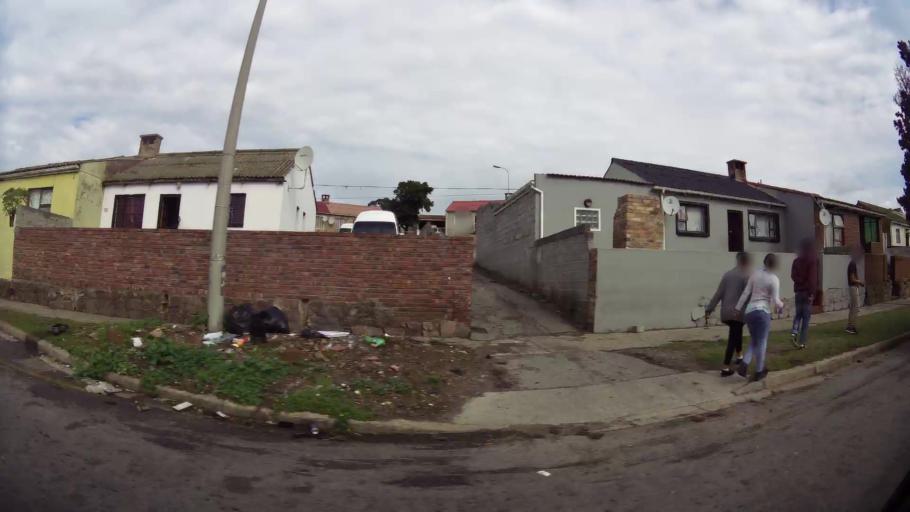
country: ZA
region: Eastern Cape
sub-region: Nelson Mandela Bay Metropolitan Municipality
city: Port Elizabeth
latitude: -33.9347
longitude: 25.5784
